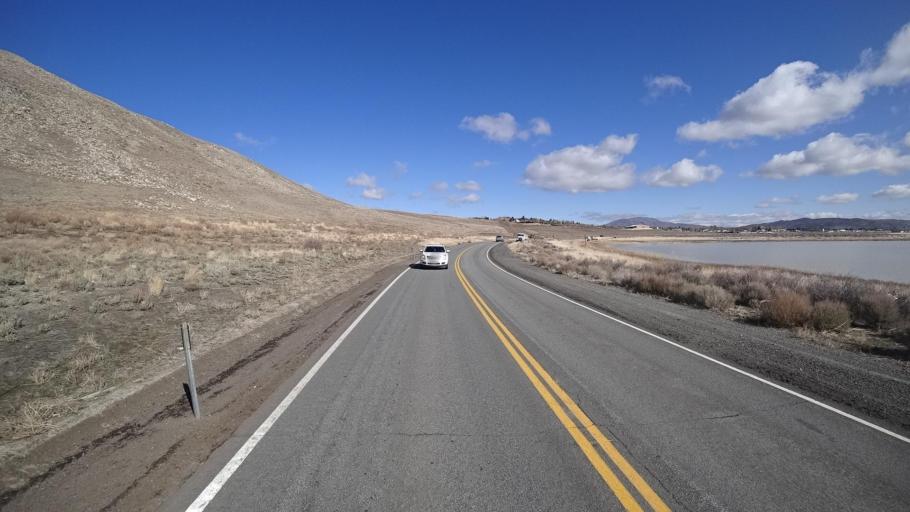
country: US
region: Nevada
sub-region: Washoe County
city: Cold Springs
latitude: 39.6489
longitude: -119.9276
